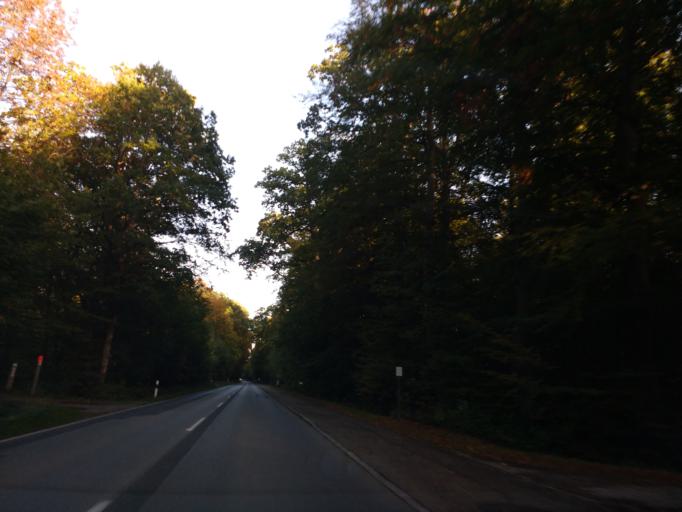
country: DE
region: Schleswig-Holstein
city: Kellenhusen
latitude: 54.1963
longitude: 11.0362
